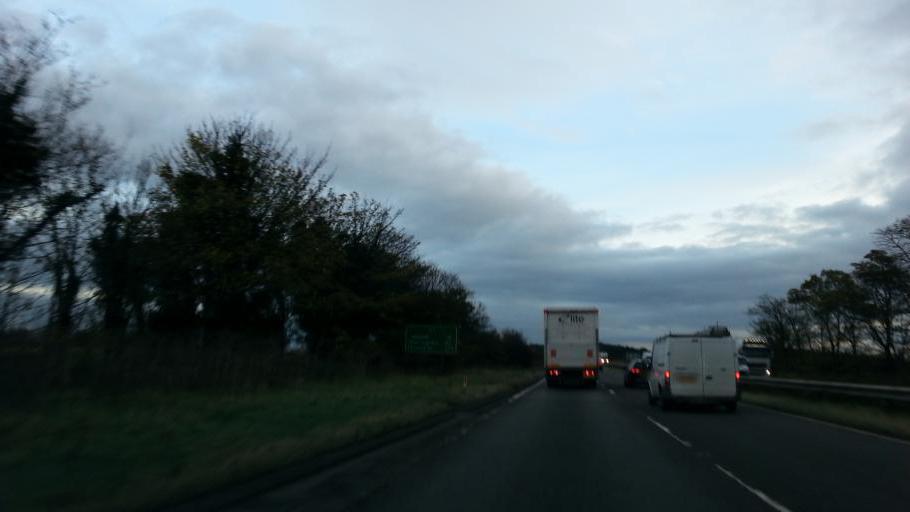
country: GB
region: England
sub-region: Nottinghamshire
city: Bircotes
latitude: 53.3635
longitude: -1.0508
